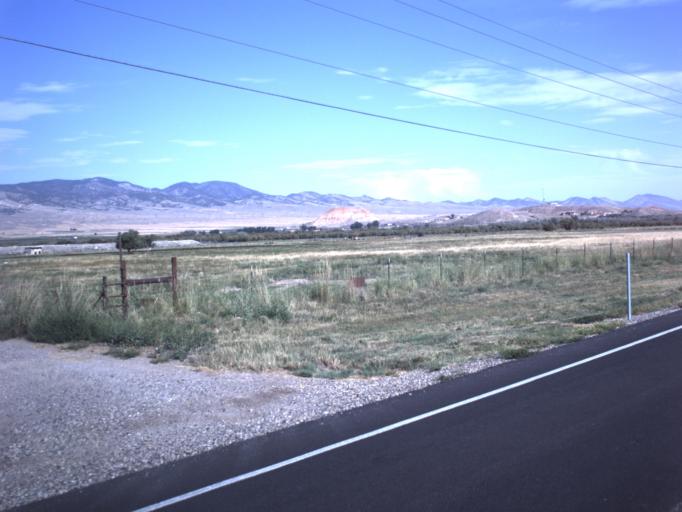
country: US
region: Utah
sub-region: Sevier County
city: Salina
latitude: 38.9816
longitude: -111.8606
